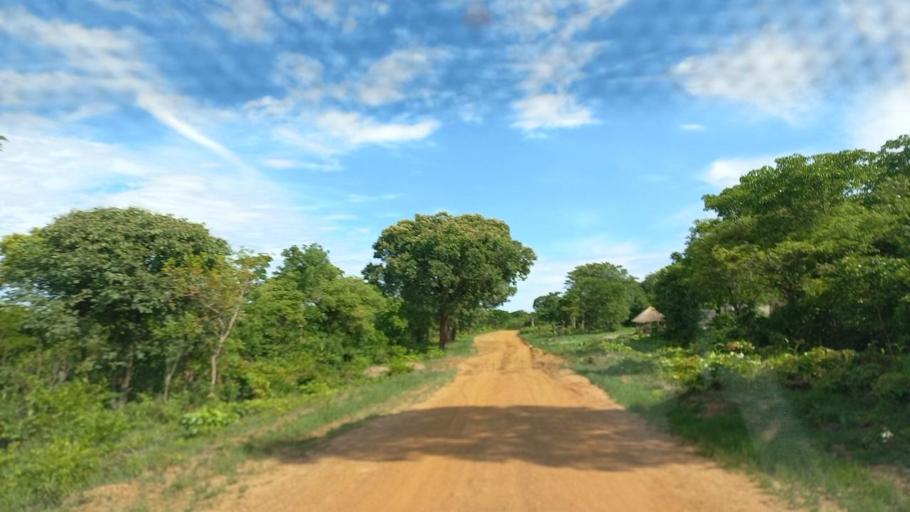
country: ZM
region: North-Western
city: Kabompo
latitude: -13.0737
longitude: 24.2182
